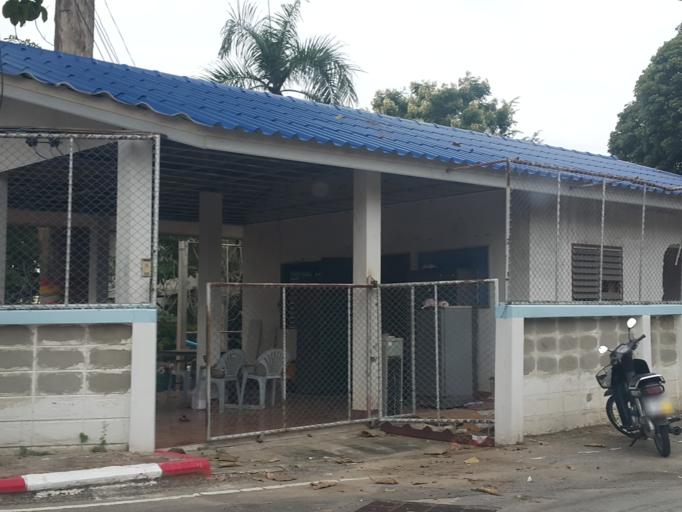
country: TH
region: Lampang
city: Lampang
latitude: 18.2919
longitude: 99.5052
